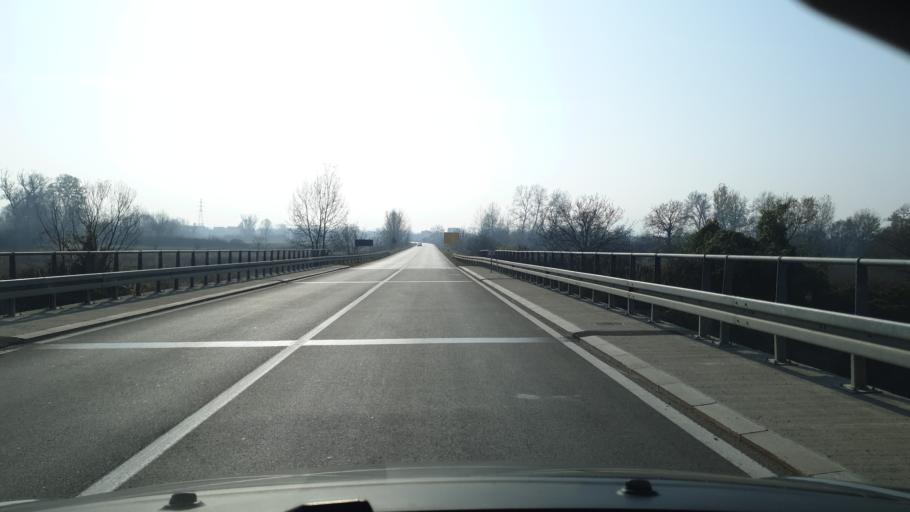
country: RS
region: Central Serbia
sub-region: Zajecarski Okrug
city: Zajecar
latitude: 43.9200
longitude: 22.2947
